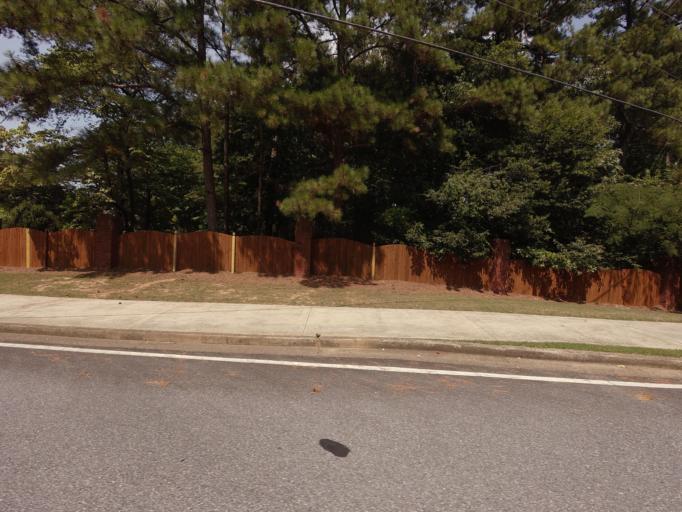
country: US
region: Georgia
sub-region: Fulton County
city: Johns Creek
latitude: 34.0091
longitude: -84.2633
